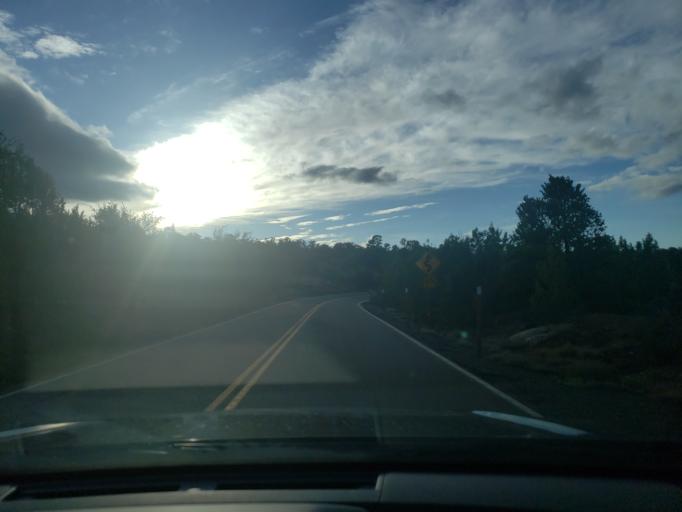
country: US
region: Colorado
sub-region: Mesa County
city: Redlands
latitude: 39.0270
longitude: -108.6615
